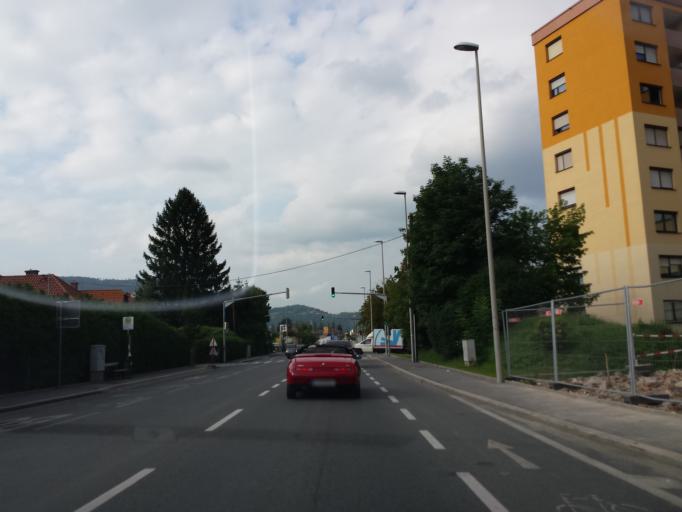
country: AT
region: Styria
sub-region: Graz Stadt
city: Wetzelsdorf
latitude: 47.0556
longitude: 15.3953
